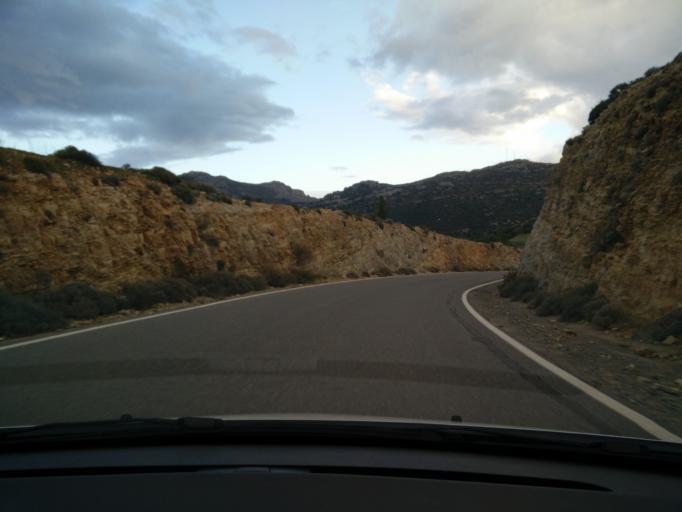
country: GR
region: Crete
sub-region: Nomos Lasithiou
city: Gra Liyia
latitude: 35.0876
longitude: 25.7059
